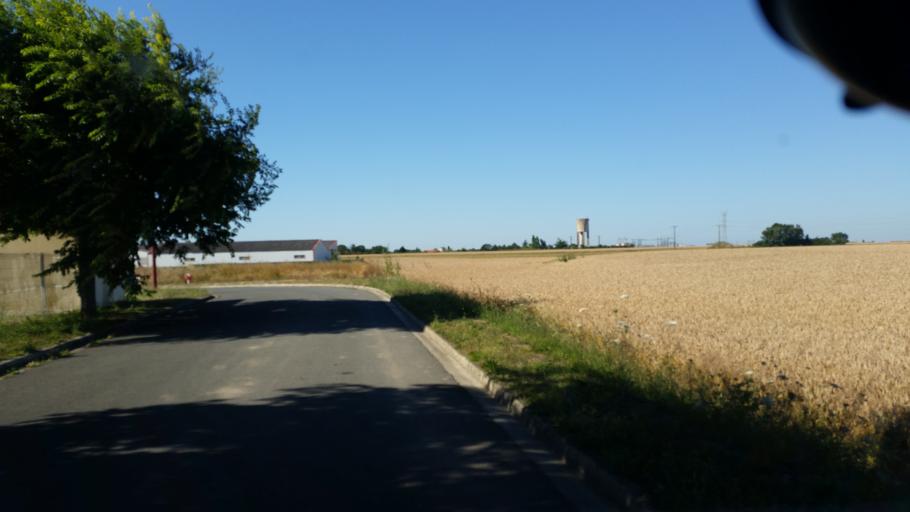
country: FR
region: Poitou-Charentes
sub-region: Departement de la Charente-Maritime
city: Marans
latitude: 46.2951
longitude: -0.9895
